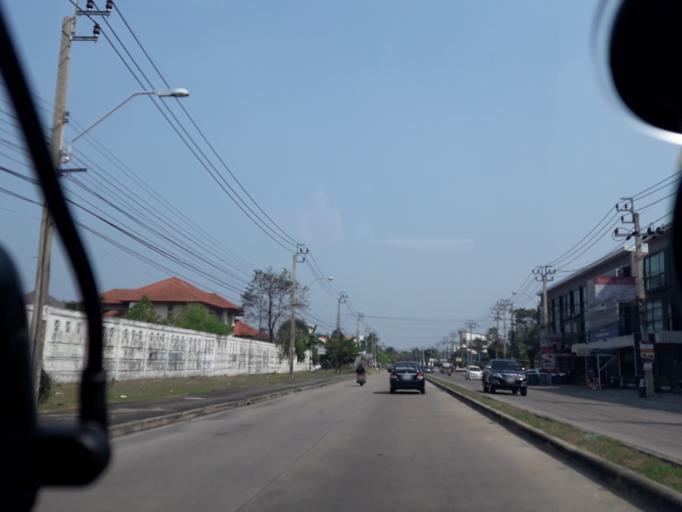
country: TH
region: Bangkok
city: Khlong Sam Wa
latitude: 13.8528
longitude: 100.7035
